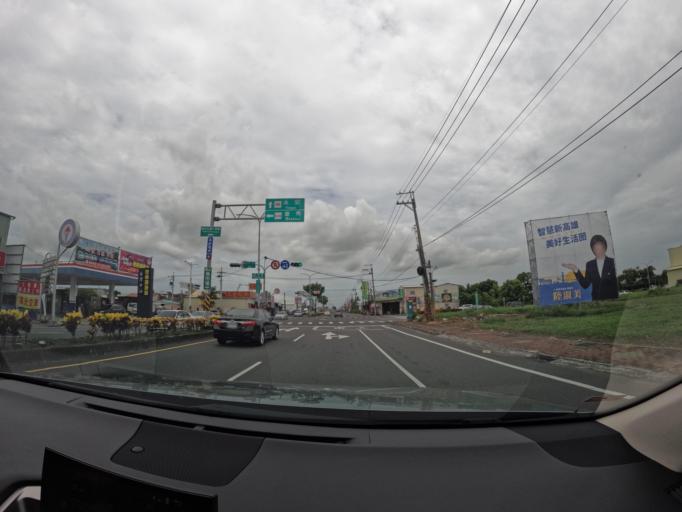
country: TW
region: Taiwan
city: Fengshan
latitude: 22.7864
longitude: 120.3136
